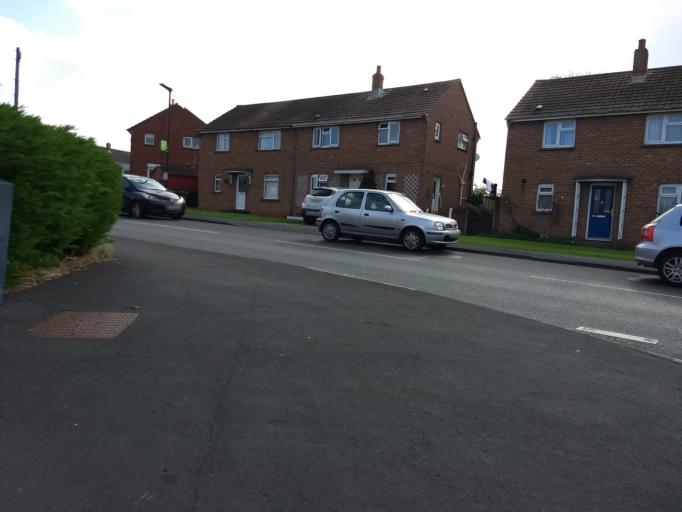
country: GB
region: England
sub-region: Isle of Wight
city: Newport
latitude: 50.6977
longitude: -1.2853
